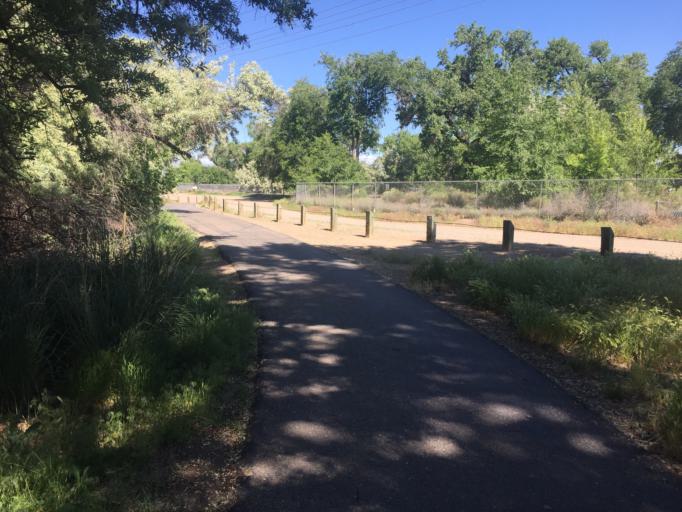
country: US
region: Colorado
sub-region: Mesa County
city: Grand Junction
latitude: 39.0674
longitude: -108.5916
